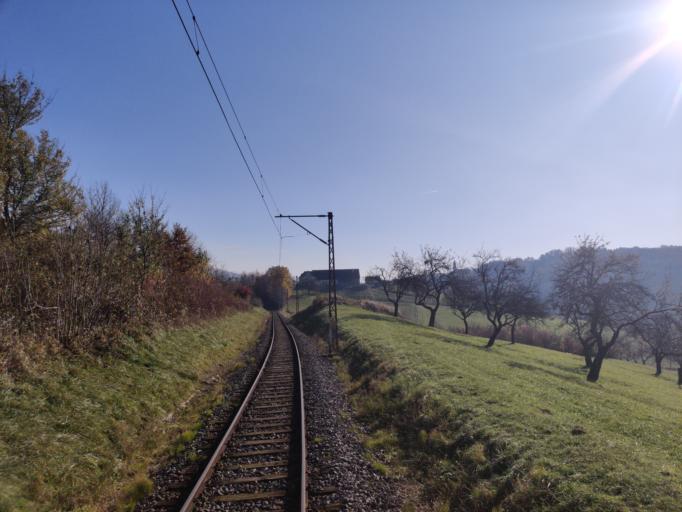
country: AT
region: Styria
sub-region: Politischer Bezirk Suedoststeiermark
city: Trautmannsdorf in Oststeiermark
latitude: 46.8817
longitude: 15.8832
